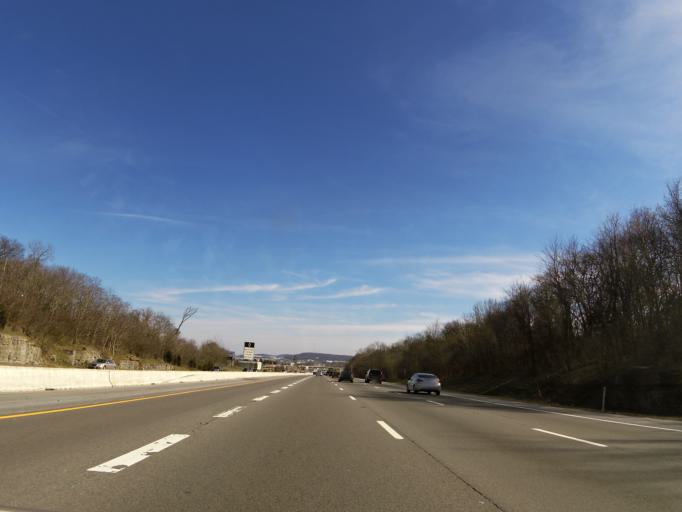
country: US
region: Tennessee
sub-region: Rutherford County
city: La Vergne
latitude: 36.0214
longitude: -86.6286
